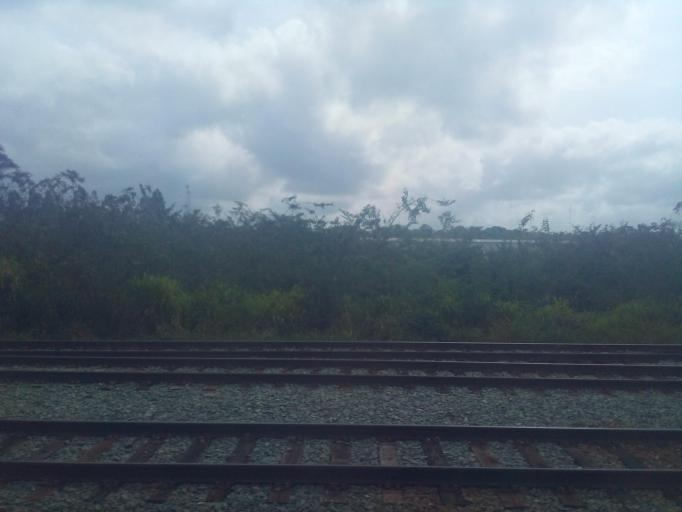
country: BR
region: Maranhao
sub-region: Icatu
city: Icatu
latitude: -2.9194
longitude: -44.3527
